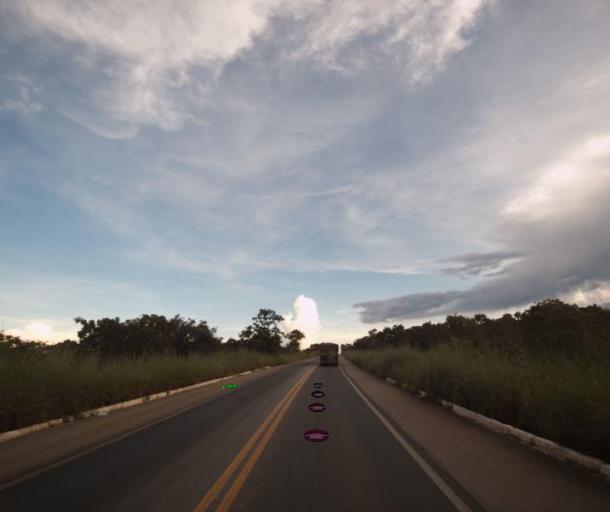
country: BR
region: Goias
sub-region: Uruacu
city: Uruacu
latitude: -14.2295
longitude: -49.1336
